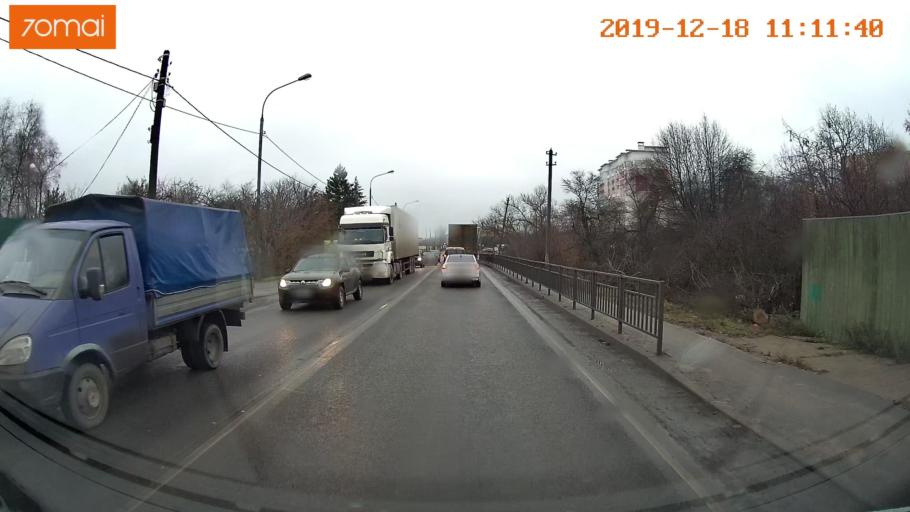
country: RU
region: Moskovskaya
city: Krasnoznamensk
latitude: 55.6254
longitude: 37.0203
